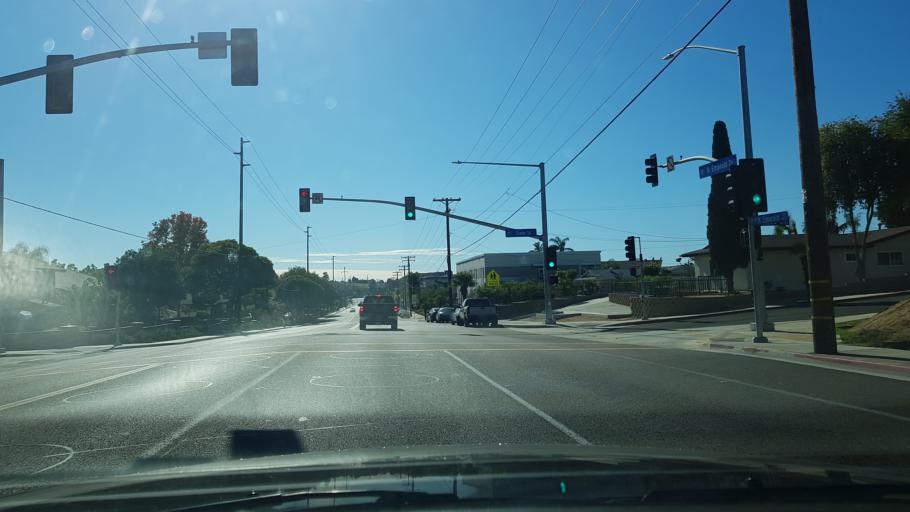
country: US
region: California
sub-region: San Diego County
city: Vista
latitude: 33.1938
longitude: -117.2796
